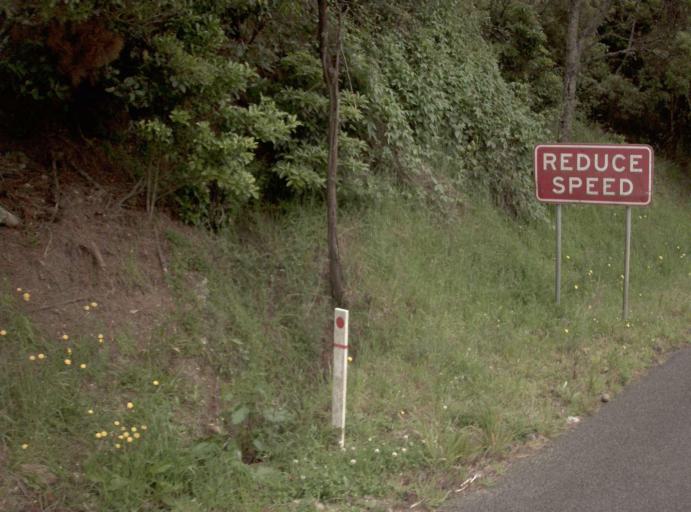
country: AU
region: Victoria
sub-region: Latrobe
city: Morwell
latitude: -38.6280
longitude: 146.1822
